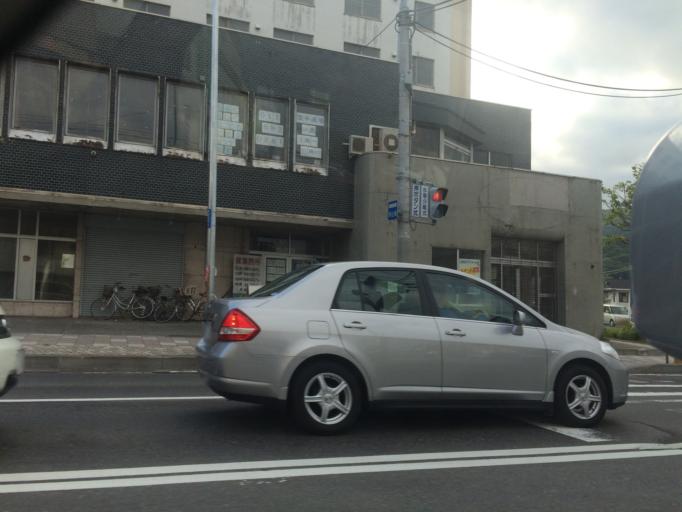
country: JP
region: Hokkaido
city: Sapporo
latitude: 43.0051
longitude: 141.3480
